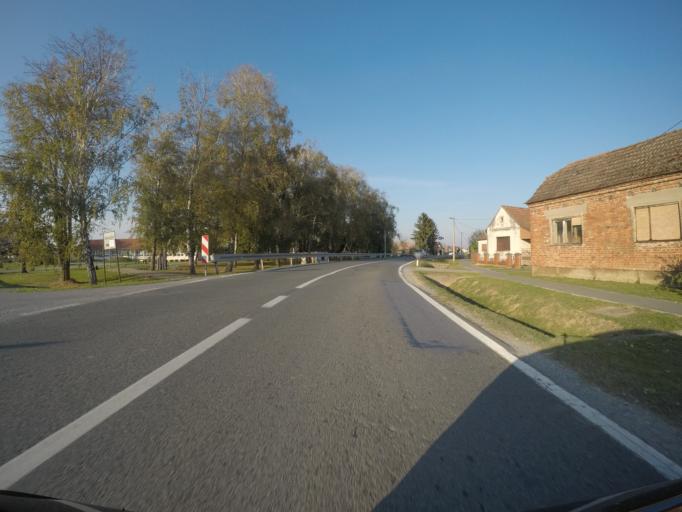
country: HU
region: Somogy
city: Barcs
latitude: 45.9092
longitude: 17.4411
